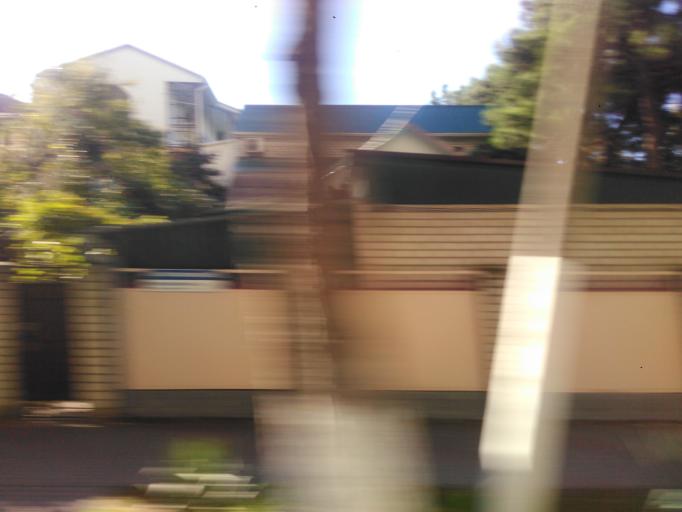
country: RU
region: Krasnodarskiy
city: Gelendzhik
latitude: 44.5529
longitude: 38.0665
